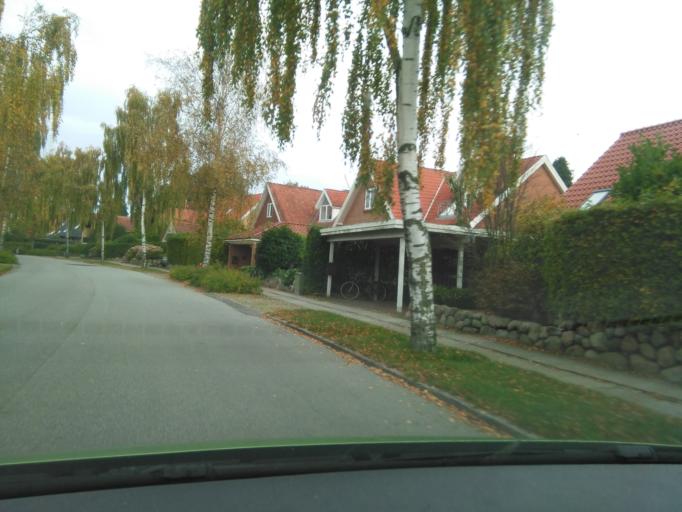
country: DK
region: Central Jutland
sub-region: Arhus Kommune
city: Arhus
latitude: 56.1174
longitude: 10.1883
